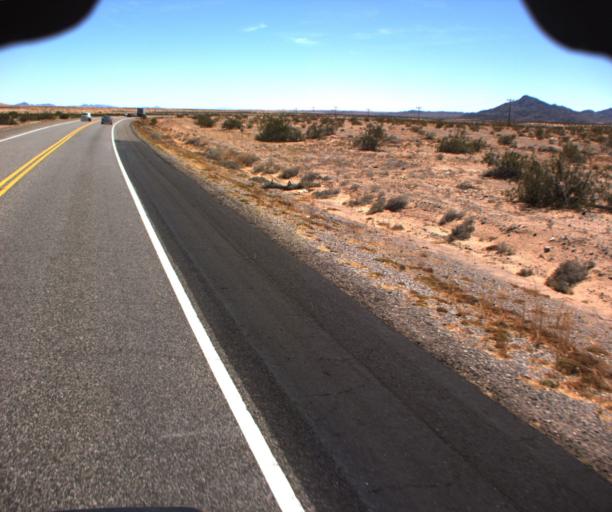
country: US
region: Arizona
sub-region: La Paz County
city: Parker
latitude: 34.0695
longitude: -114.2592
